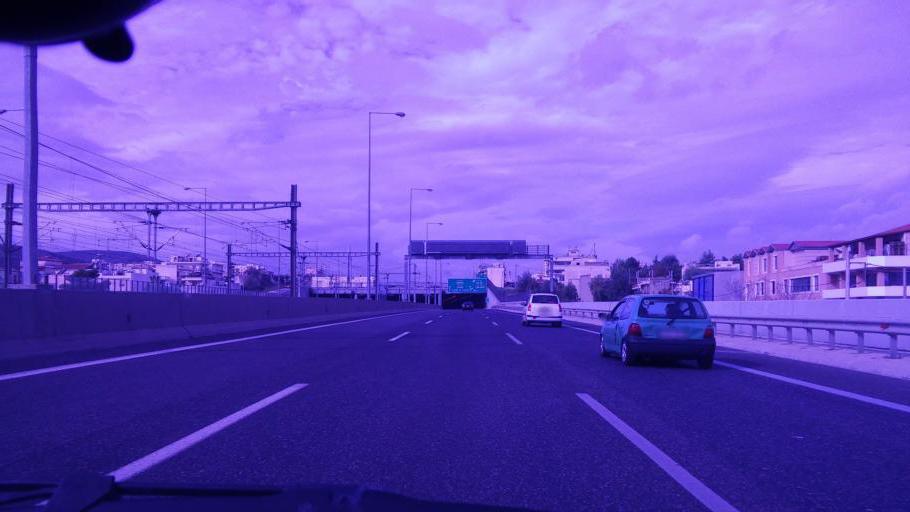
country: GR
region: Attica
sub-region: Nomarchia Dytikis Attikis
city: Zefyri
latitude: 38.0692
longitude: 23.7221
